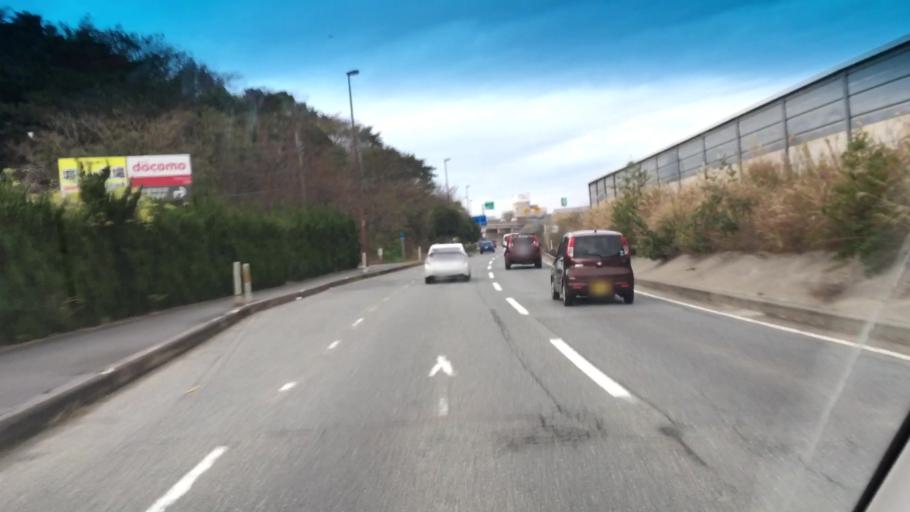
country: JP
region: Fukuoka
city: Maebaru-chuo
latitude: 33.5705
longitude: 130.2893
